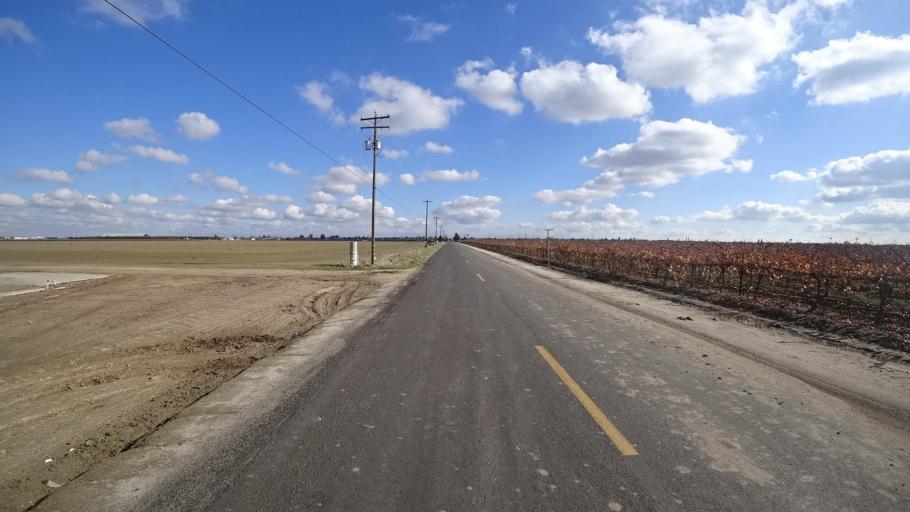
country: US
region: California
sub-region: Kern County
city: McFarland
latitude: 35.6816
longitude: -119.2495
